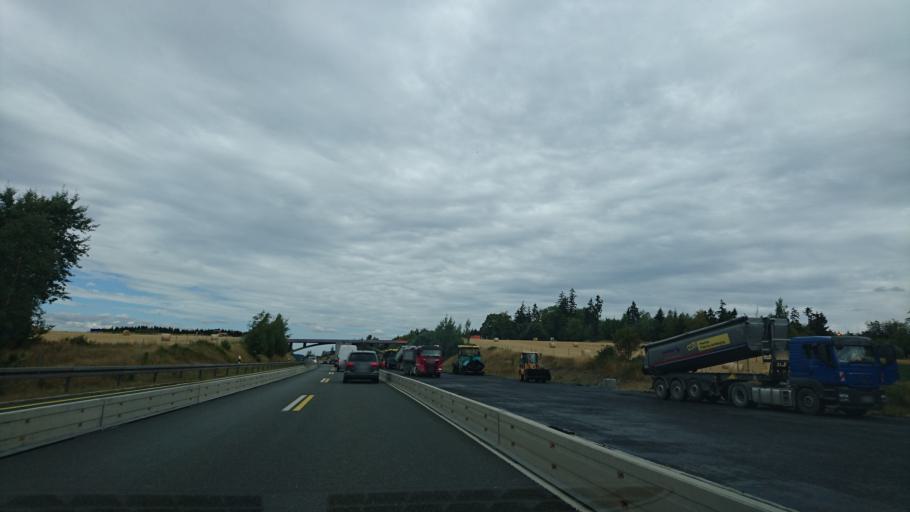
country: DE
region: Bavaria
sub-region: Upper Franconia
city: Gattendorf
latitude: 50.3265
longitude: 12.0227
